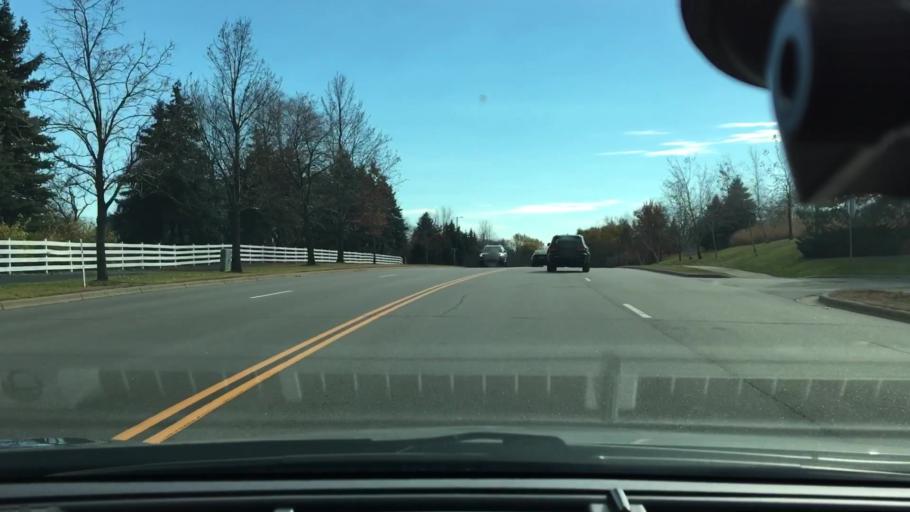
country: US
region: Minnesota
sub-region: Hennepin County
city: Maple Grove
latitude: 45.1144
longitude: -93.4922
